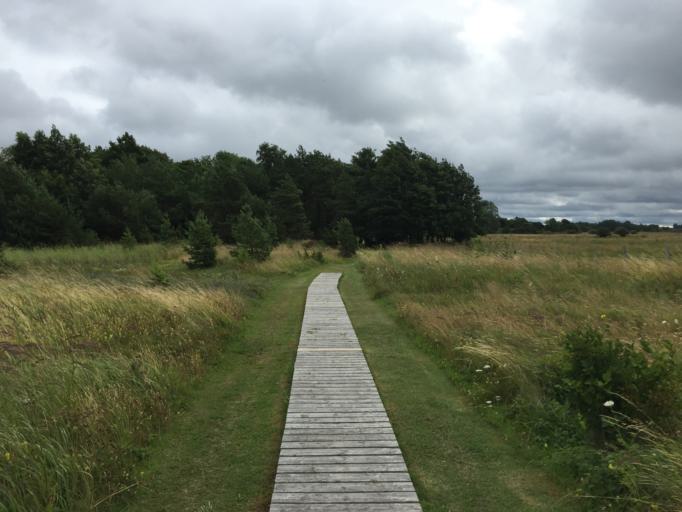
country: SE
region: Gotland
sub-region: Gotland
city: Klintehamn
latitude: 57.4520
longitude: 18.1275
